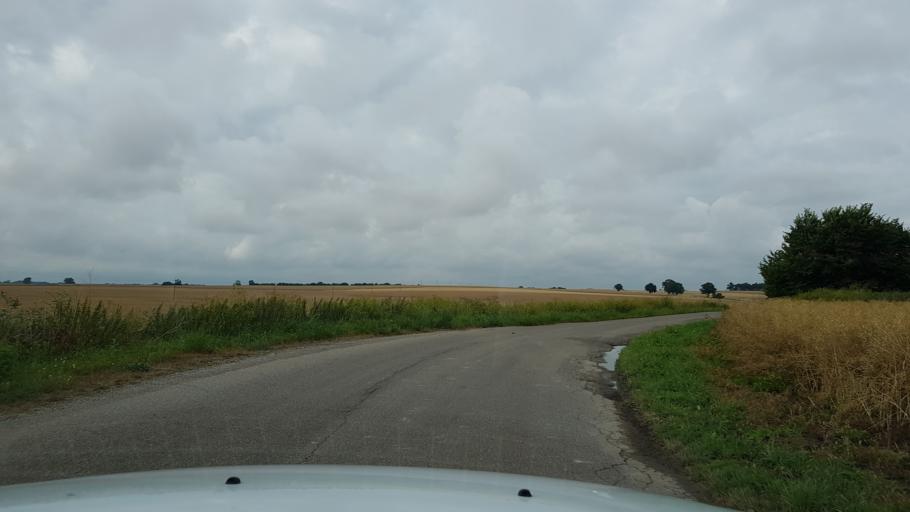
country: PL
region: West Pomeranian Voivodeship
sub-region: Powiat pyrzycki
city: Przelewice
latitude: 53.0857
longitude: 15.1456
